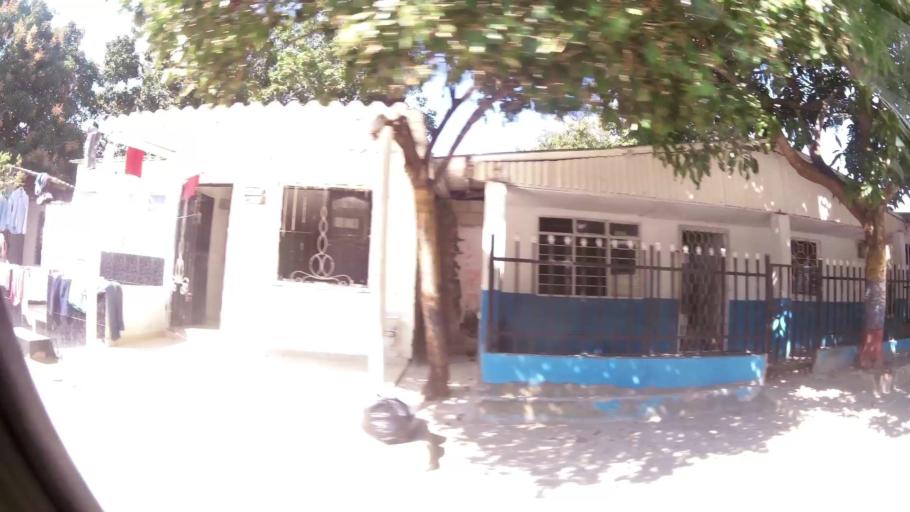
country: CO
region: Atlantico
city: Barranquilla
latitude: 10.9325
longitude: -74.8308
